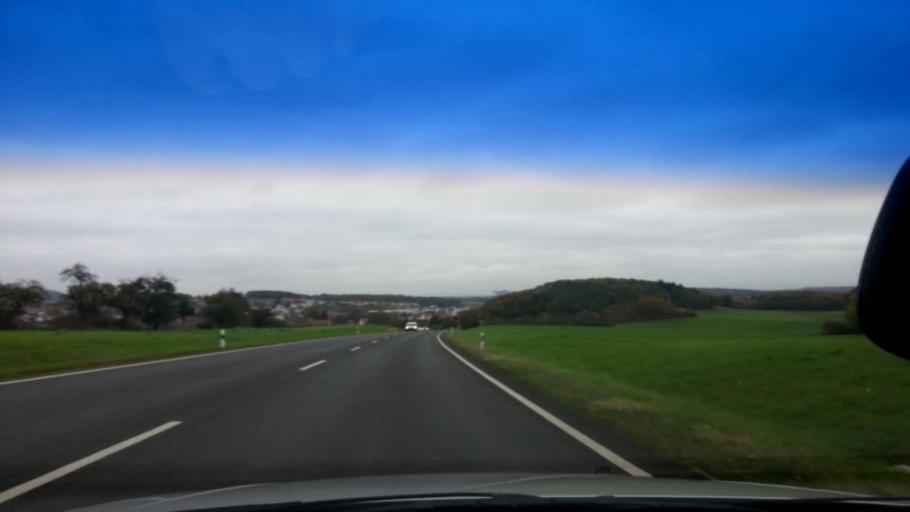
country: DE
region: Bavaria
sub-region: Upper Franconia
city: Stegaurach
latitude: 49.8515
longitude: 10.8476
